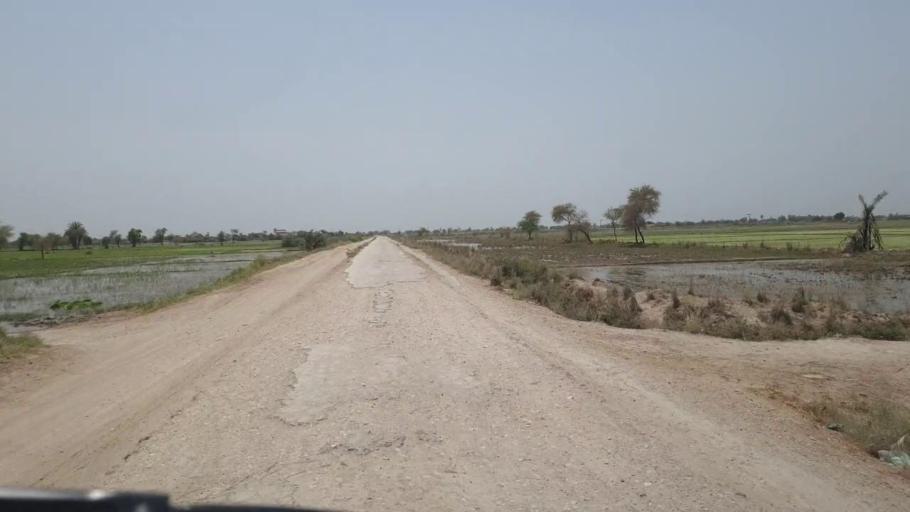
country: PK
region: Sindh
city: Daur
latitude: 26.4608
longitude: 68.1473
